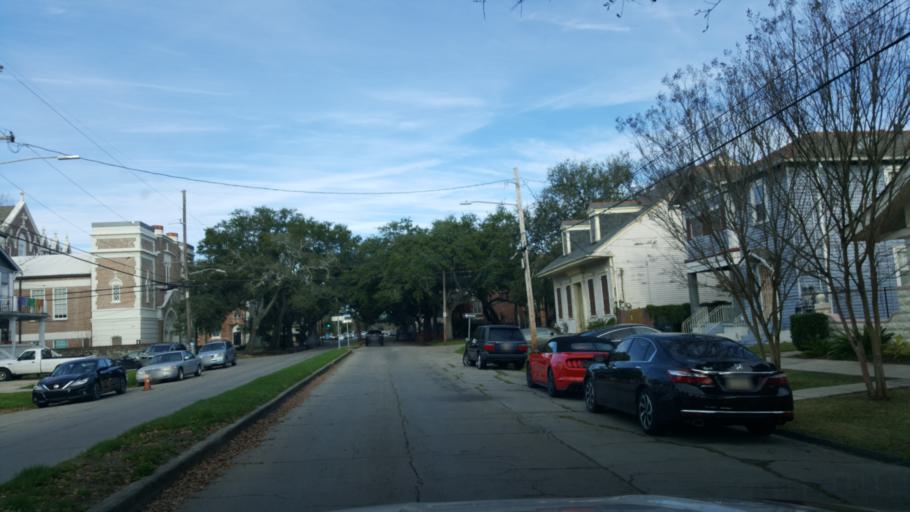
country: US
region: Louisiana
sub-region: Orleans Parish
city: New Orleans
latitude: 29.9693
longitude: -90.0735
